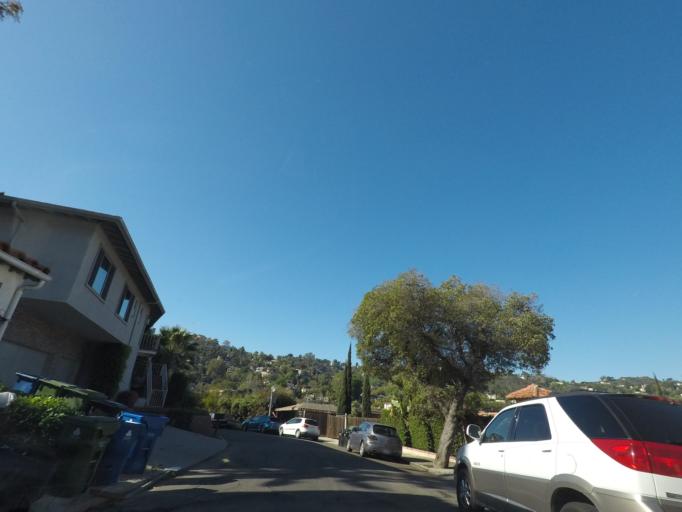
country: US
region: California
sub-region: Los Angeles County
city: Universal City
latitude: 34.1292
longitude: -118.3457
